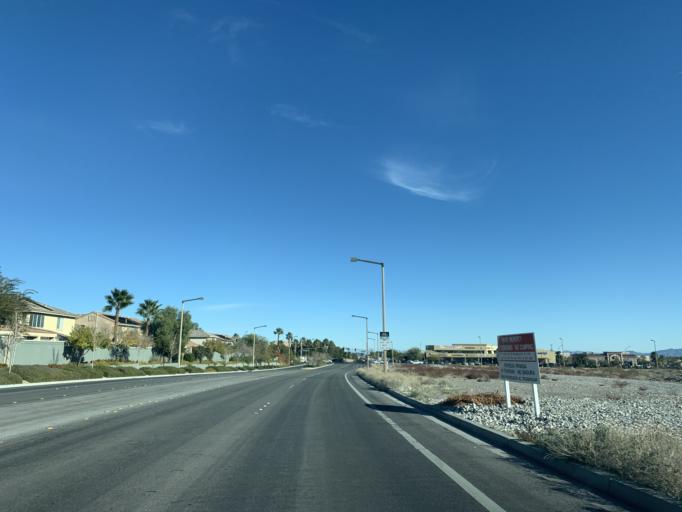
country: US
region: Nevada
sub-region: Clark County
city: Summerlin South
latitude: 36.1224
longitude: -115.3177
